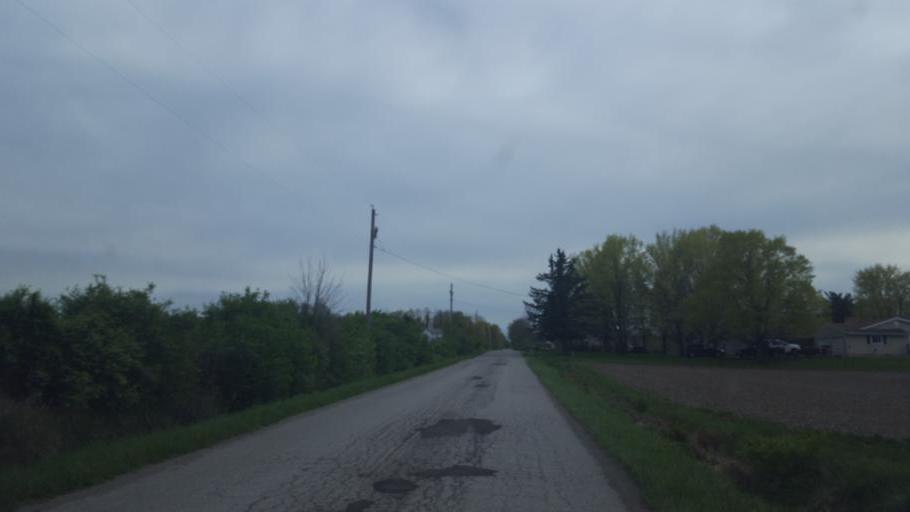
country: US
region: Ohio
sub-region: Crawford County
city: Crestline
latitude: 40.6968
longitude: -82.6893
